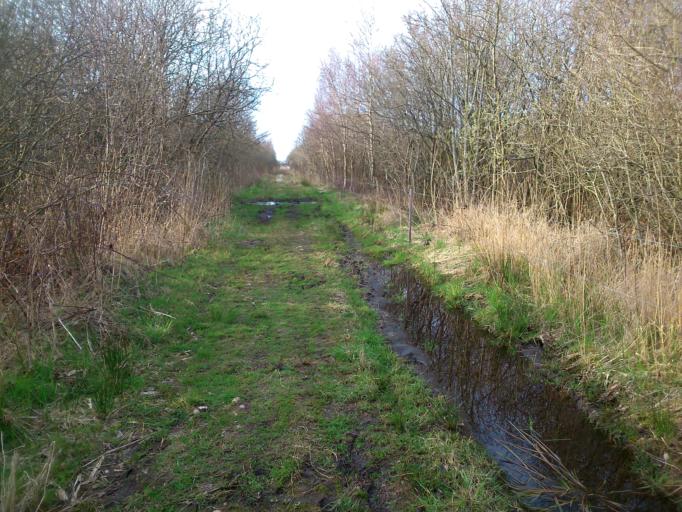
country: DK
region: South Denmark
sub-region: Tonder Kommune
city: Tonder
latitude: 55.0298
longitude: 8.8357
